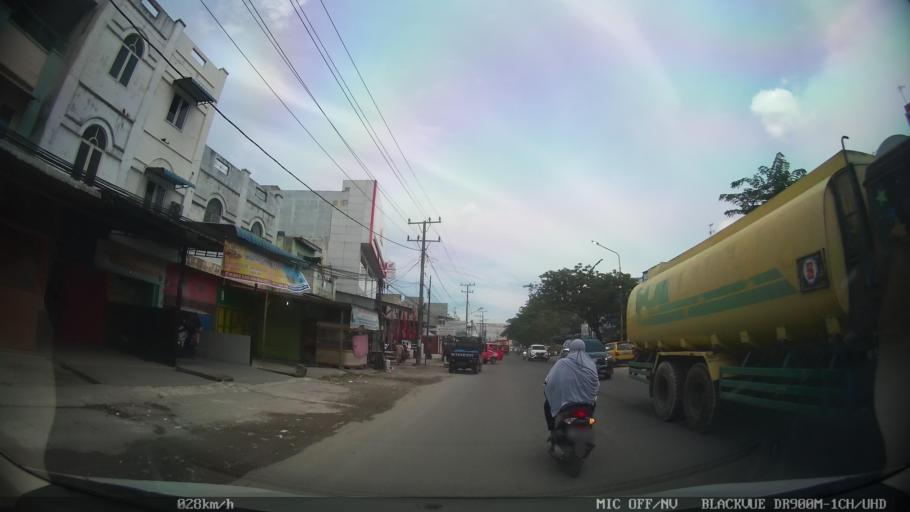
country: ID
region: North Sumatra
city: Labuhan Deli
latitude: 3.7119
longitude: 98.6609
